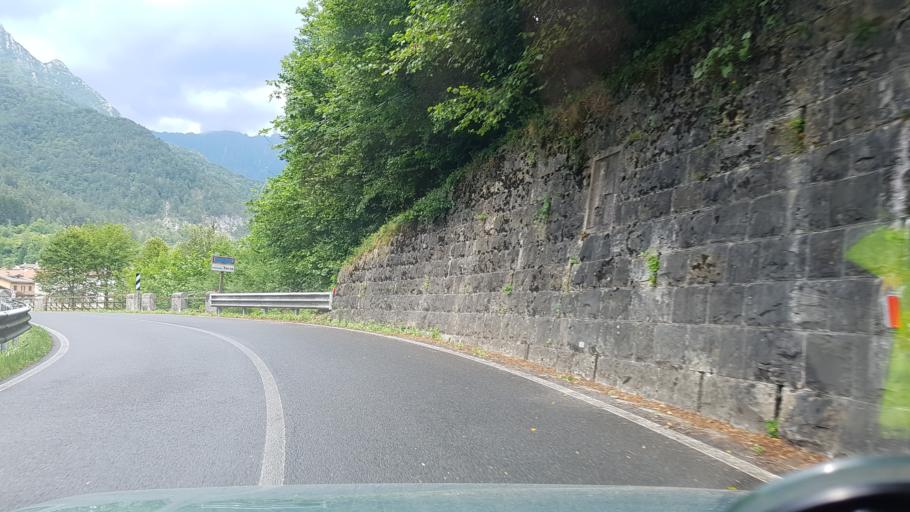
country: IT
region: Friuli Venezia Giulia
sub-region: Provincia di Udine
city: Lusevera
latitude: 46.2763
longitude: 13.2610
